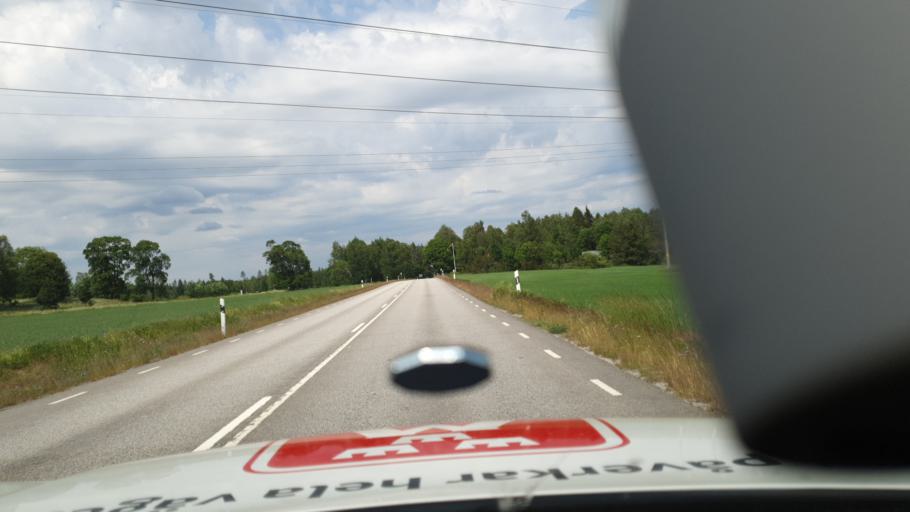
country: SE
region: Joenkoeping
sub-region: Varnamo Kommun
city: Varnamo
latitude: 57.2182
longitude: 14.0405
